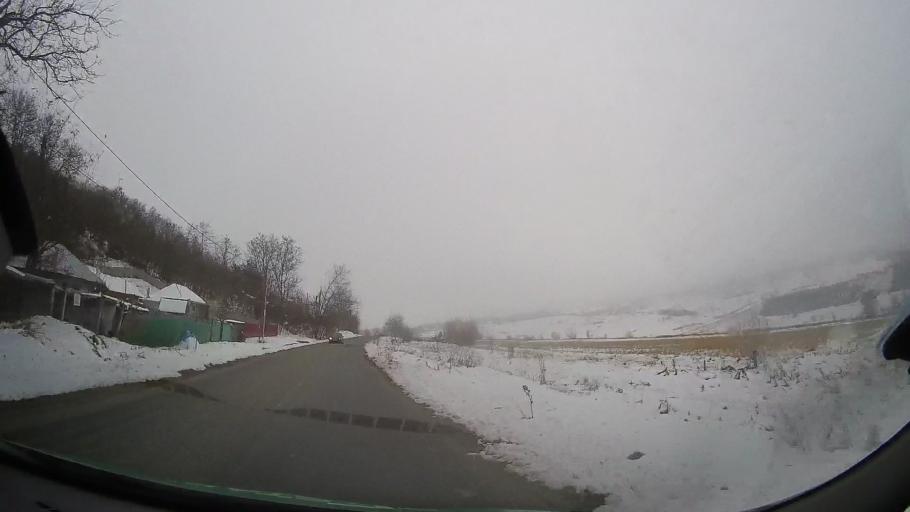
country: RO
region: Bacau
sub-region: Comuna Vultureni
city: Vultureni
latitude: 46.3400
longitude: 27.2907
